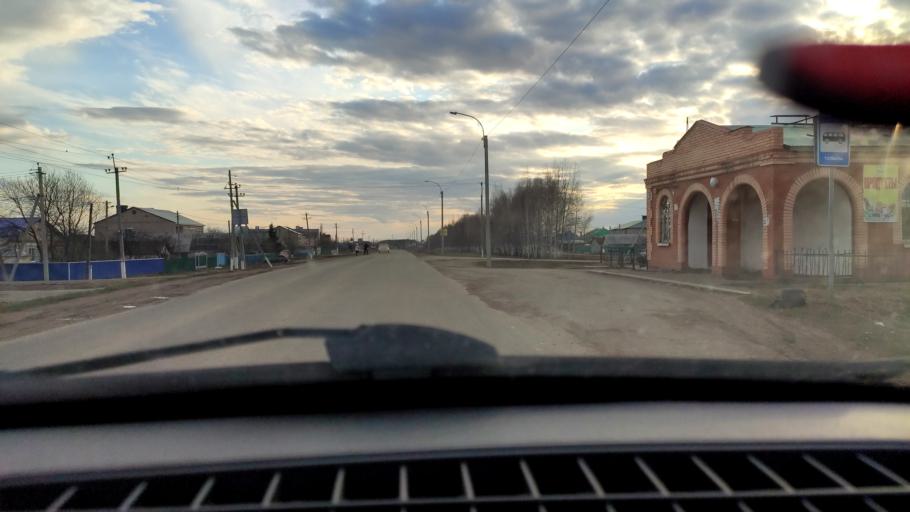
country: RU
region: Bashkortostan
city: Tolbazy
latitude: 54.0052
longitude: 55.8682
